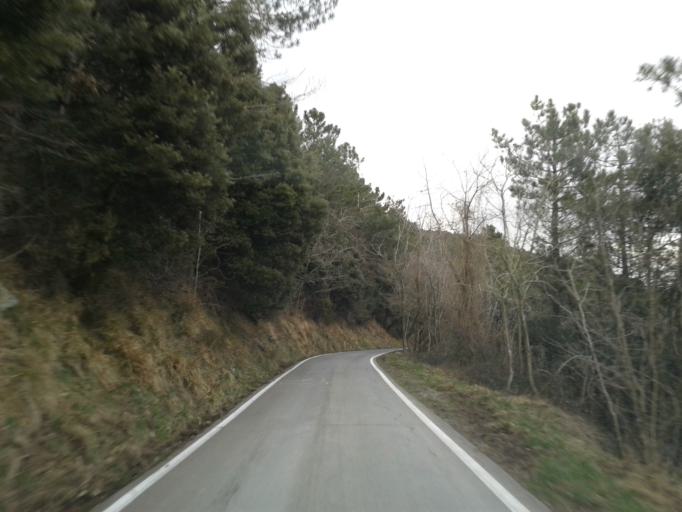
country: IT
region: Tuscany
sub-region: Province of Pisa
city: Calci
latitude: 43.7531
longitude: 10.5428
